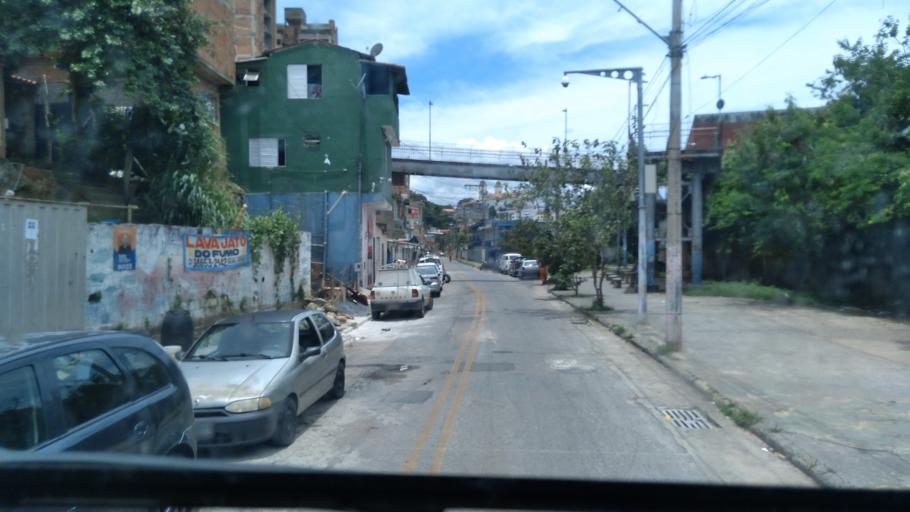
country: BR
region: Minas Gerais
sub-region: Belo Horizonte
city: Belo Horizonte
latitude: -19.9196
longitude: -43.9229
